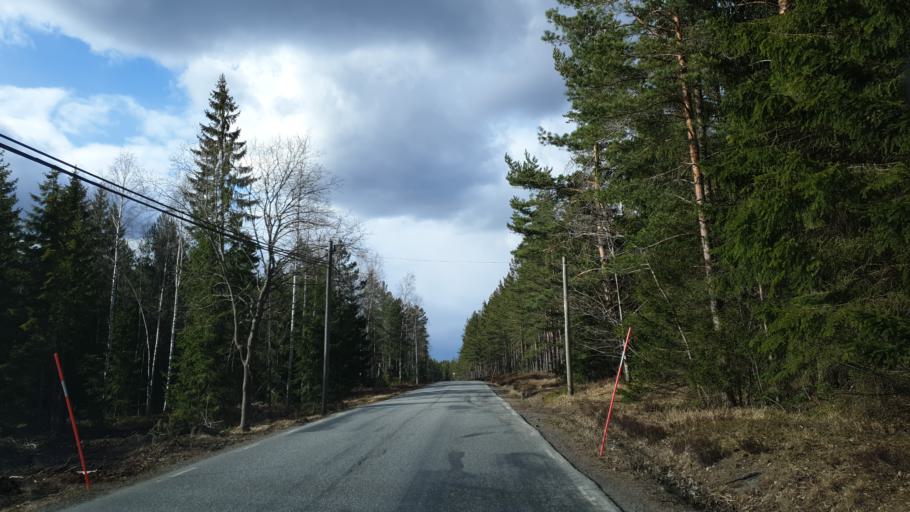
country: SE
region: Stockholm
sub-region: Tyreso Kommun
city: Brevik
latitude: 59.2506
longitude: 18.4399
